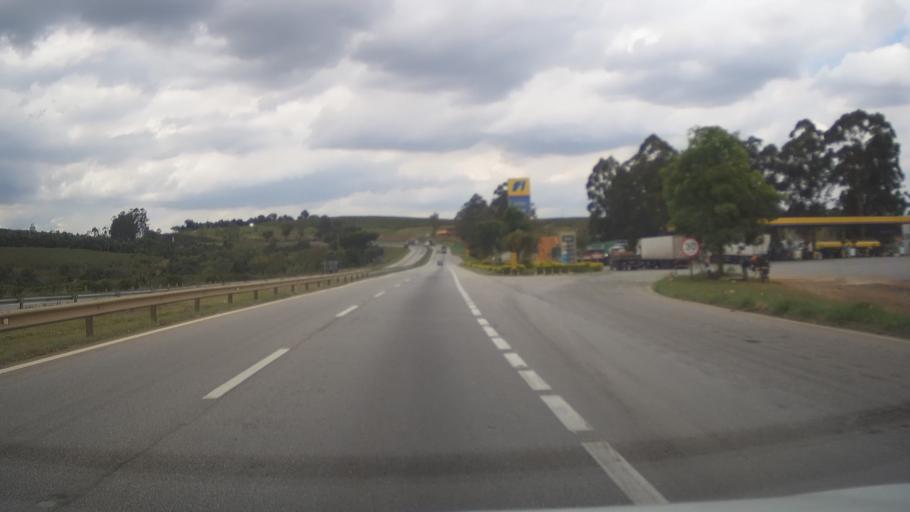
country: BR
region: Minas Gerais
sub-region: Tres Coracoes
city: Tres Coracoes
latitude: -21.4840
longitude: -45.2044
